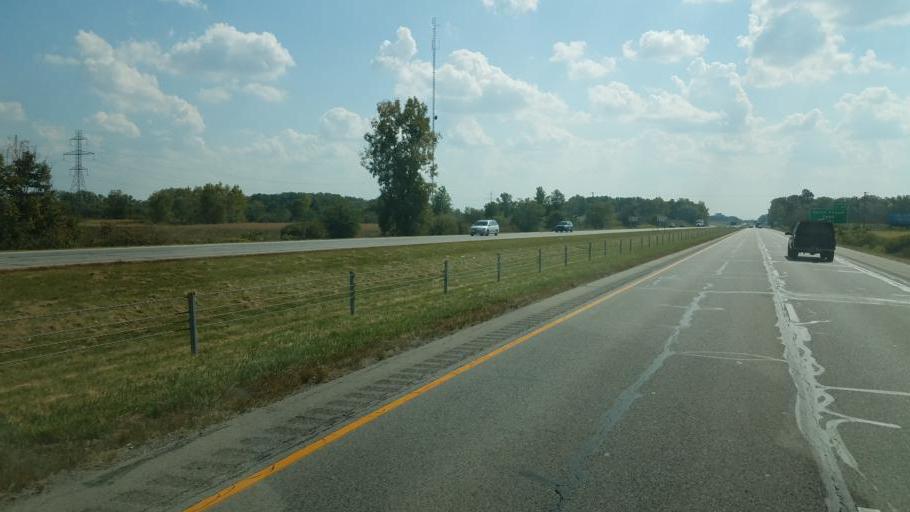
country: US
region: Indiana
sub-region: Allen County
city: Huntertown
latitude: 41.2130
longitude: -85.1048
